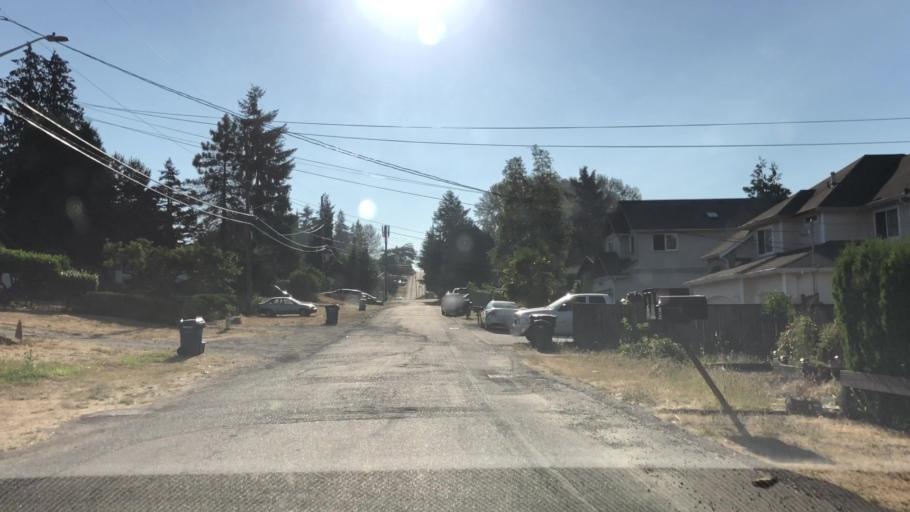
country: US
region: Washington
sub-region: King County
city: Bryn Mawr-Skyway
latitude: 47.4957
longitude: -122.2623
